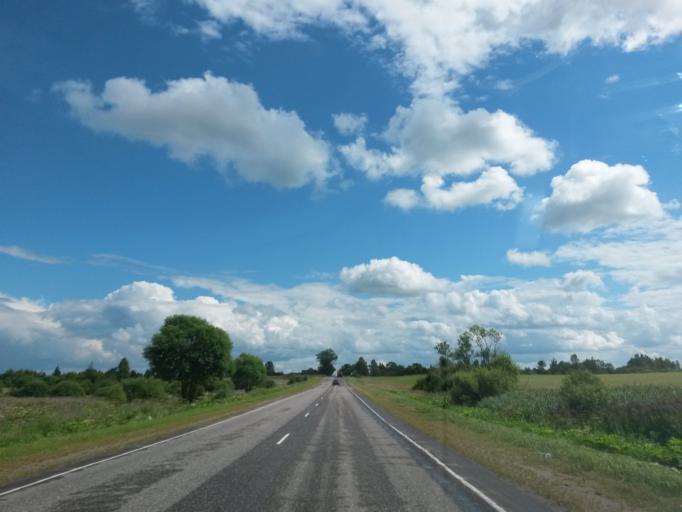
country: RU
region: Ivanovo
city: Pistsovo
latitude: 57.1920
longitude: 40.4115
